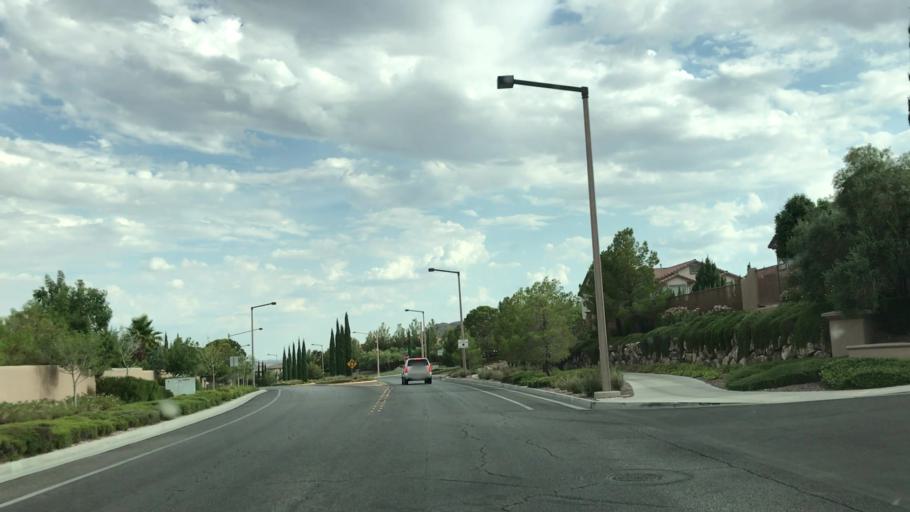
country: US
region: Nevada
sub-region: Clark County
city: Summerlin South
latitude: 36.1736
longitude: -115.3521
